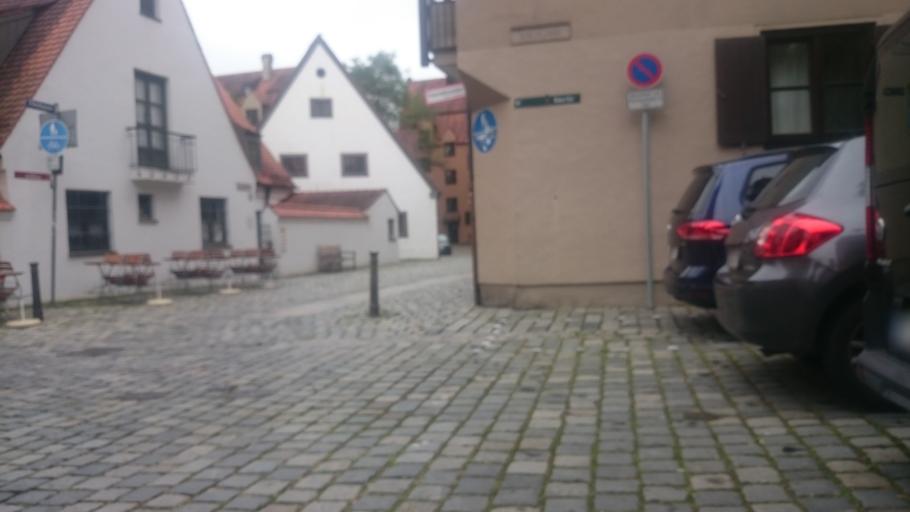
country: DE
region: Bavaria
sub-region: Swabia
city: Augsburg
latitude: 48.3609
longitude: 10.9011
